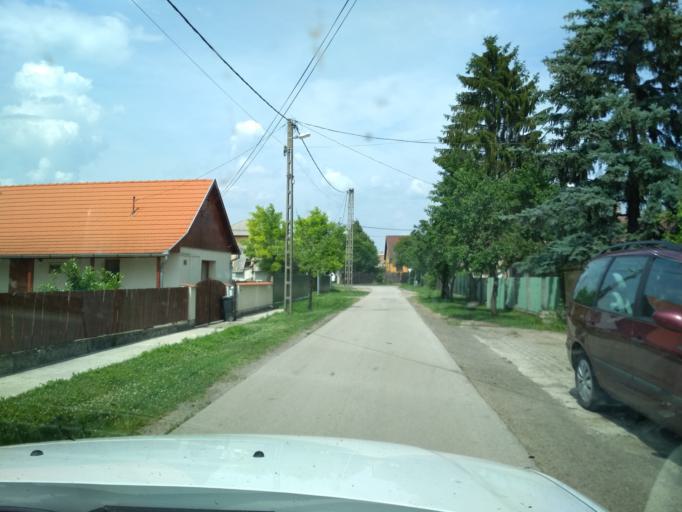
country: HU
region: Pest
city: Tapioszentmarton
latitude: 47.3400
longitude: 19.7421
